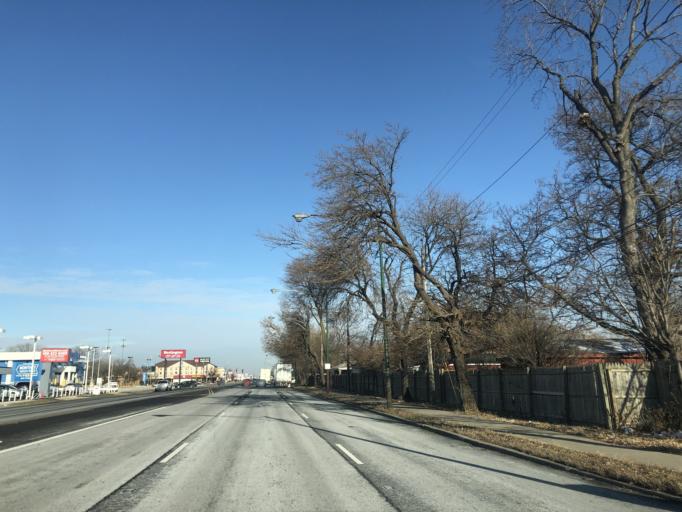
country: US
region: Illinois
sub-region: Cook County
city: Hometown
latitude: 41.7386
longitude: -87.7409
